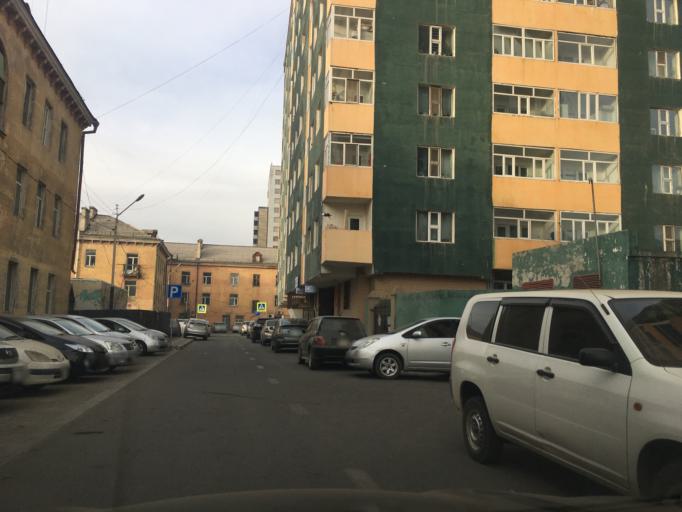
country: MN
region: Ulaanbaatar
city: Ulaanbaatar
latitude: 47.9150
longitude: 106.8785
